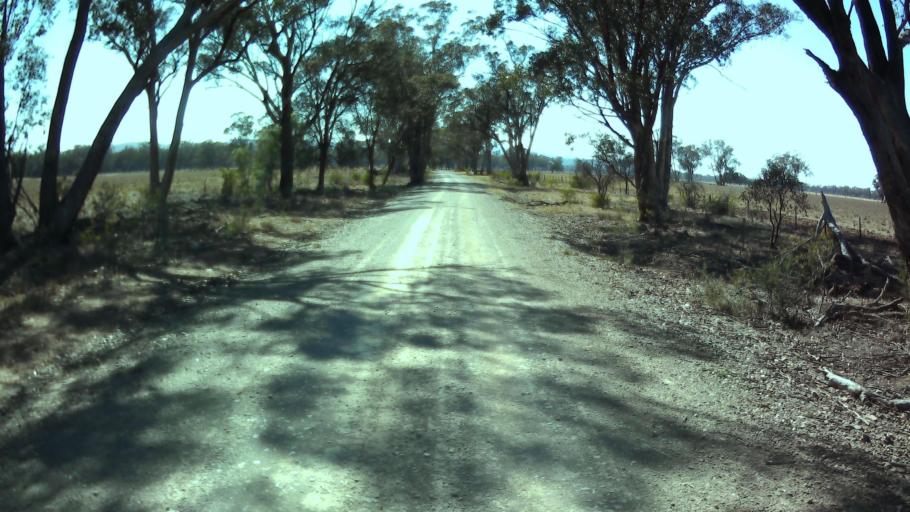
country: AU
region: New South Wales
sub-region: Weddin
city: Grenfell
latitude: -33.9447
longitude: 147.8664
